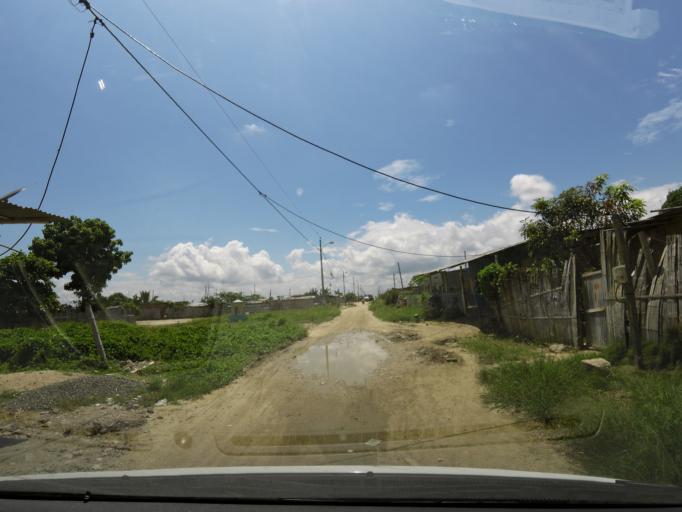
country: EC
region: El Oro
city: Huaquillas
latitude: -3.4732
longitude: -80.2117
